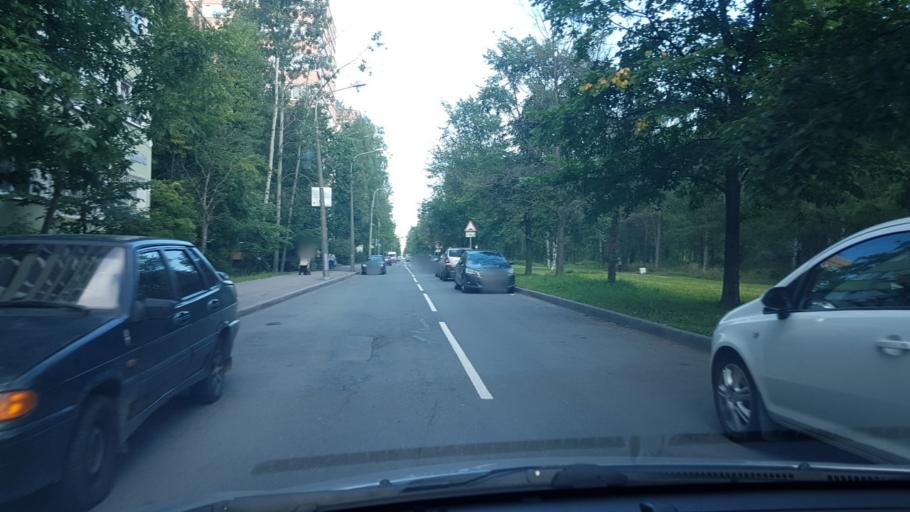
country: RU
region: St.-Petersburg
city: Dachnoye
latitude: 59.8298
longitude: 30.2280
